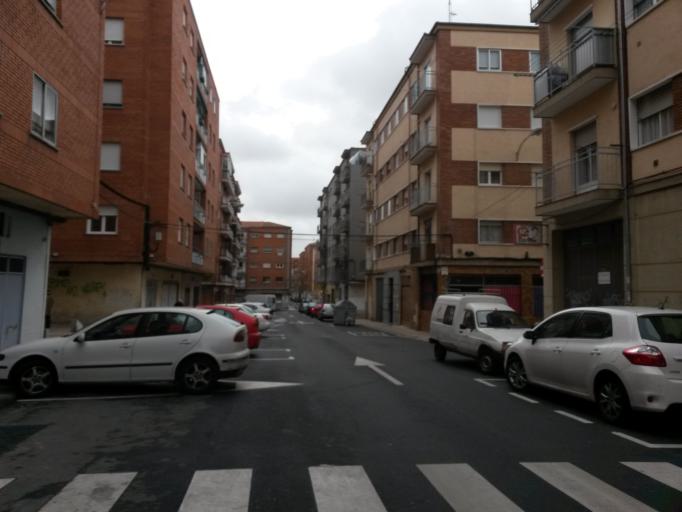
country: ES
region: Castille and Leon
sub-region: Provincia de Salamanca
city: Salamanca
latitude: 40.9778
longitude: -5.6510
